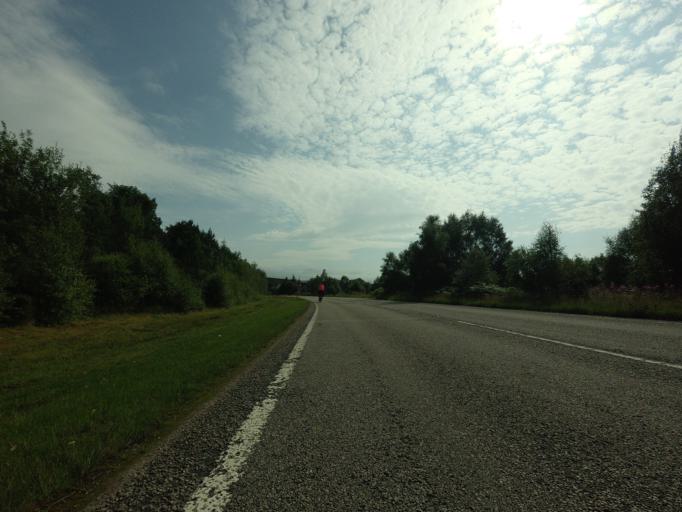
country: GB
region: Scotland
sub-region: Highland
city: Evanton
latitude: 57.9258
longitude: -4.4009
